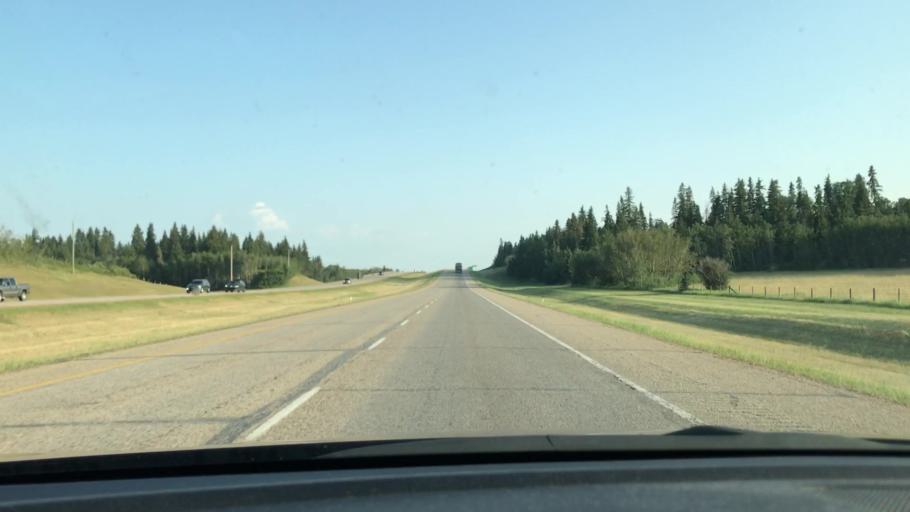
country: CA
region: Alberta
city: Ponoka
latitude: 52.5970
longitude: -113.6634
